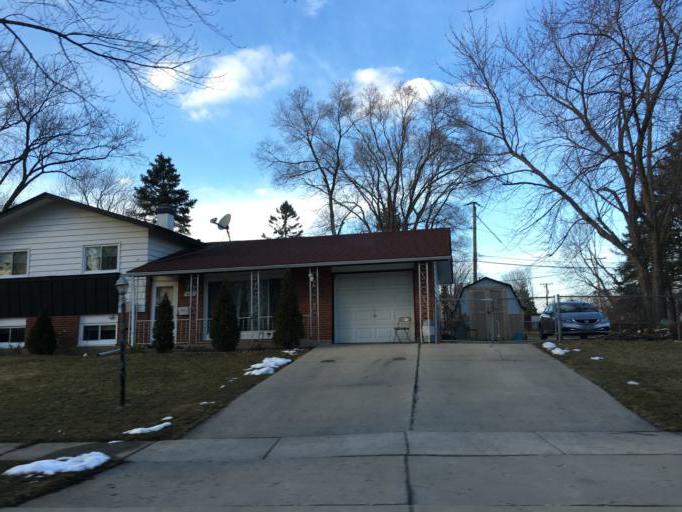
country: US
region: Illinois
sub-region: Cook County
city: Hoffman Estates
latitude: 42.0428
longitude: -88.0897
